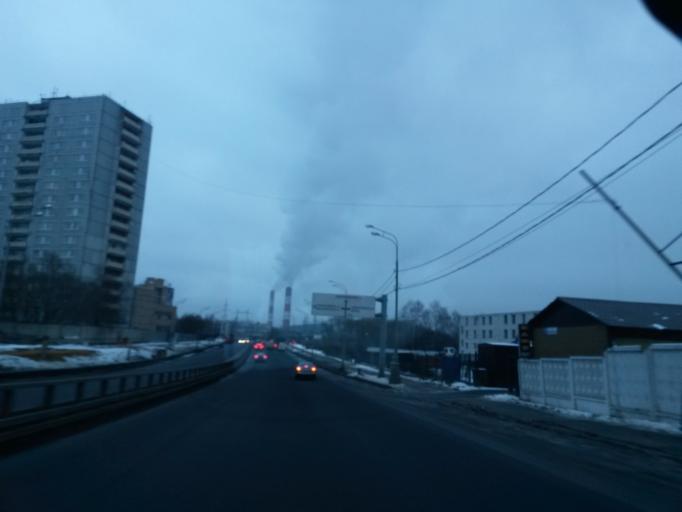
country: RU
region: Moscow
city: Mikhalkovo
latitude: 55.6850
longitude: 37.4224
